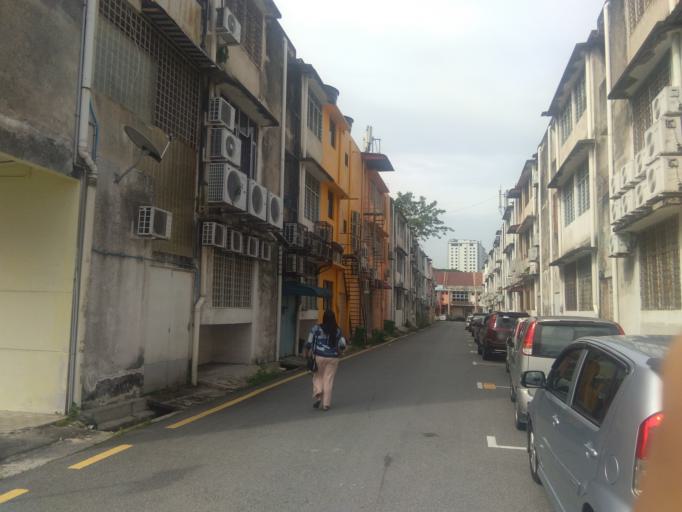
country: MY
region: Perak
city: Ipoh
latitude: 4.6075
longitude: 101.0808
